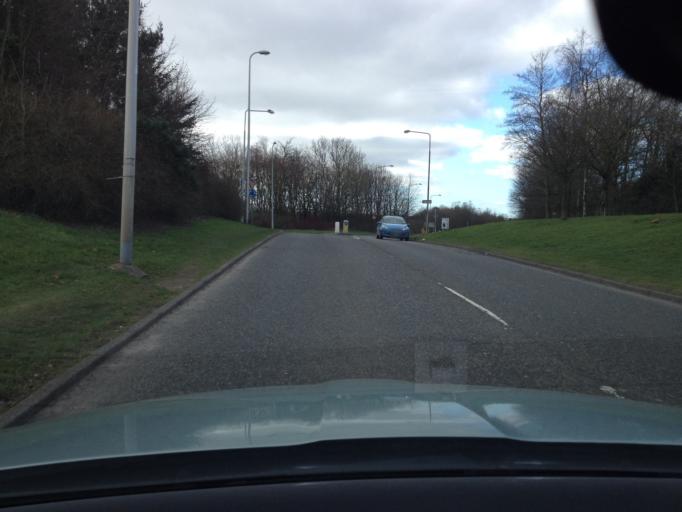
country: GB
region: Scotland
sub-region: West Lothian
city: Livingston
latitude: 55.9012
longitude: -3.5020
